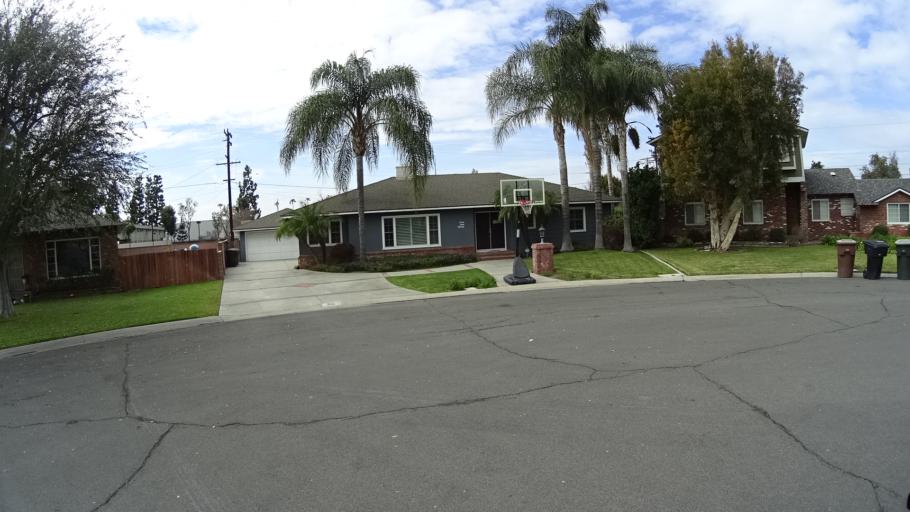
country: US
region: California
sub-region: Orange County
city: Anaheim
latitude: 33.8366
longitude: -117.9355
